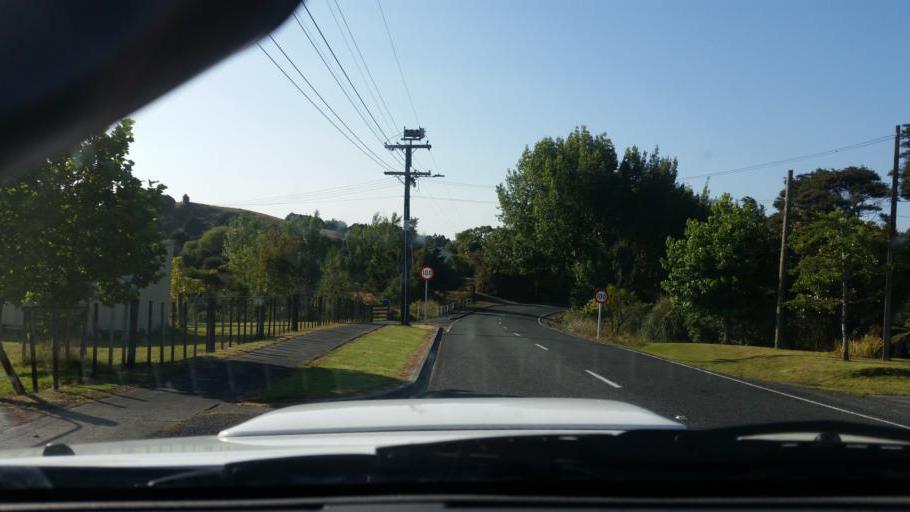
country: NZ
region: Northland
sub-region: Whangarei
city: Ruakaka
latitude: -36.1081
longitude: 174.2290
